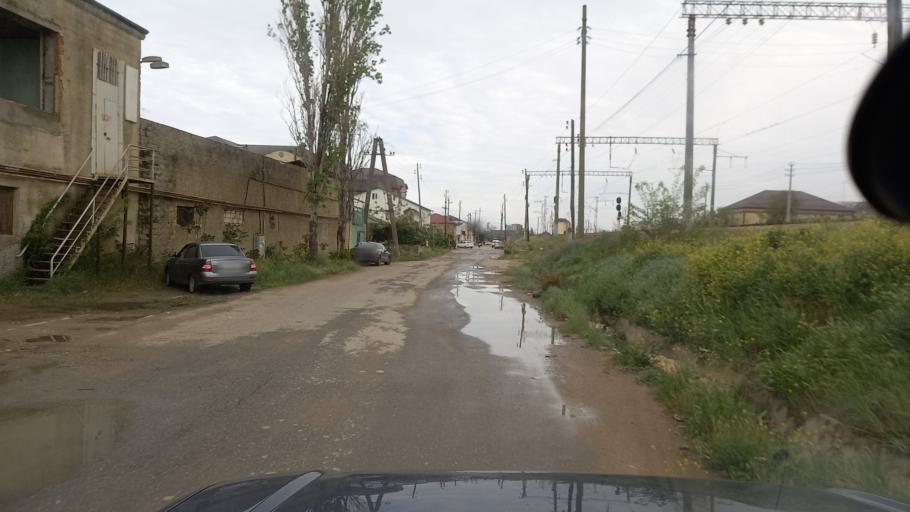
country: RU
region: Dagestan
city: Derbent
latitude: 42.0667
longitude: 48.3026
